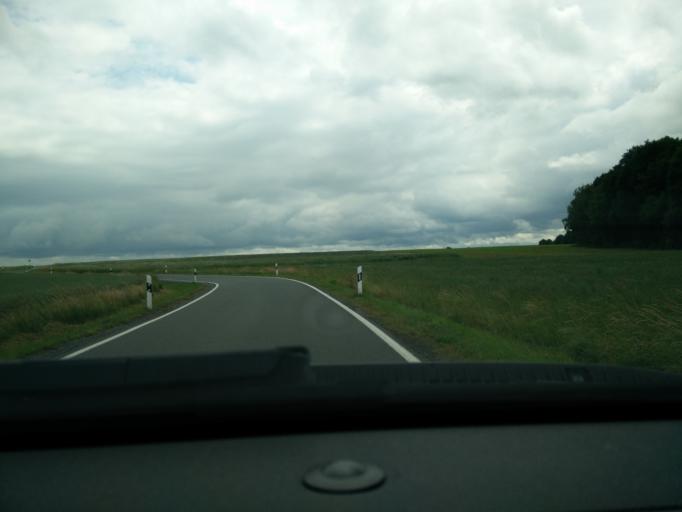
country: DE
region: Saxony
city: Bad Lausick
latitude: 51.1159
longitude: 12.6578
